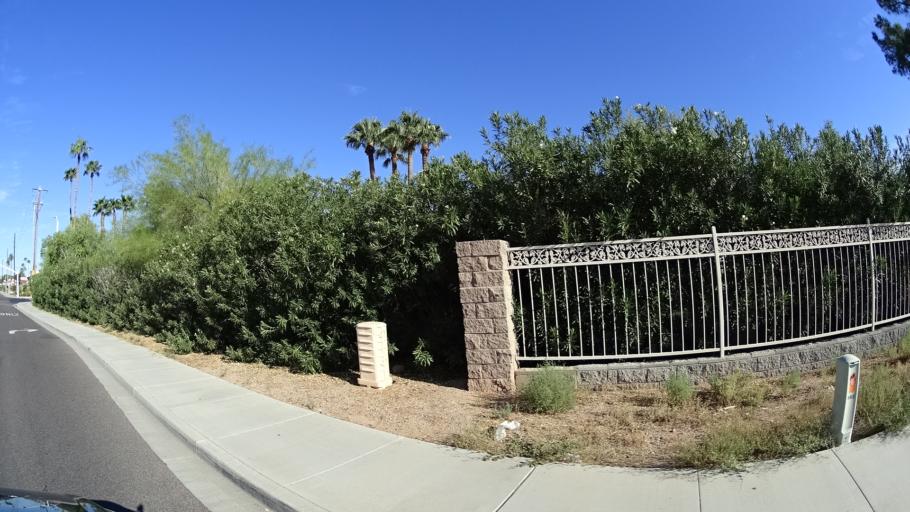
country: US
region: Arizona
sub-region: Maricopa County
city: Paradise Valley
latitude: 33.5021
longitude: -111.9426
